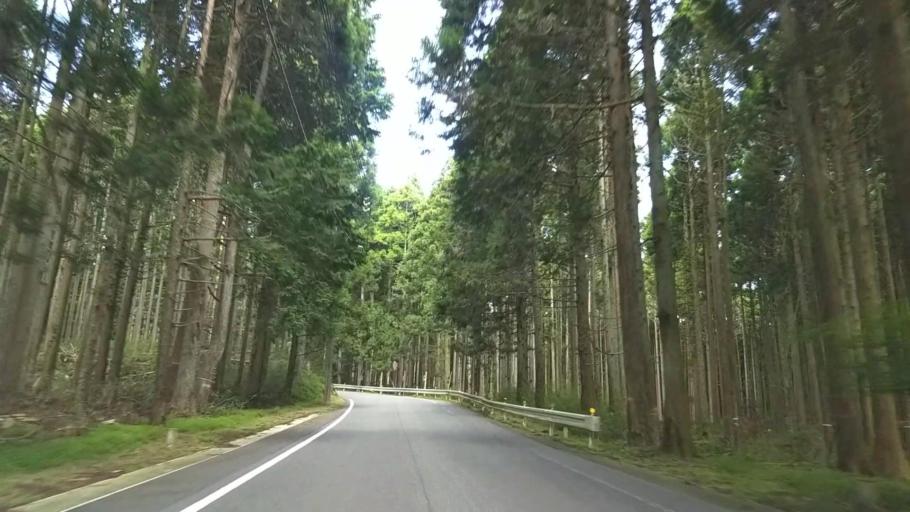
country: JP
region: Shizuoka
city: Gotemba
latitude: 35.2539
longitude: 138.8310
